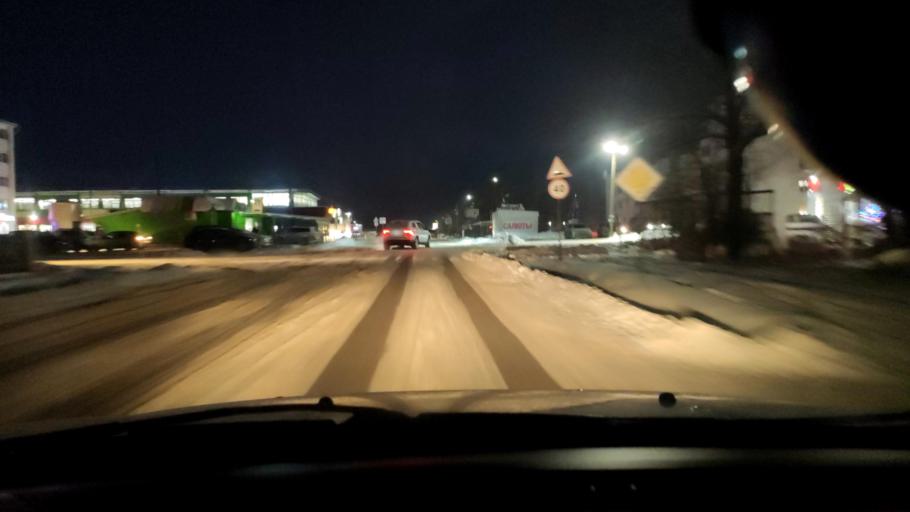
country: RU
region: Perm
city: Kultayevo
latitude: 57.8962
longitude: 55.9311
